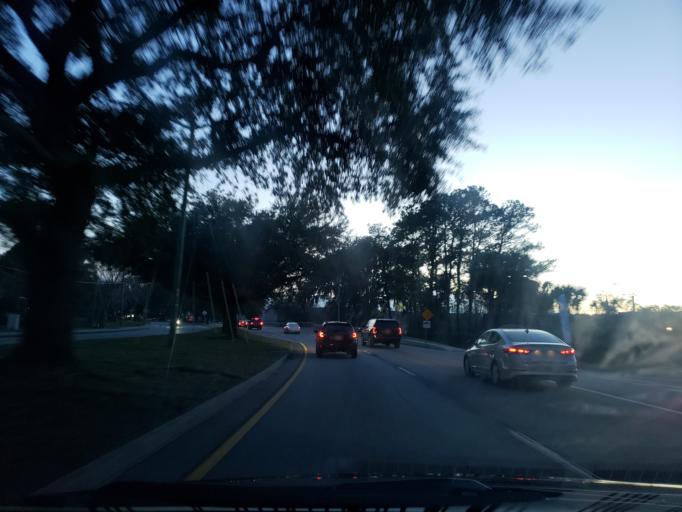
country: US
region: Georgia
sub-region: Chatham County
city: Montgomery
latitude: 31.9957
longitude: -81.1260
